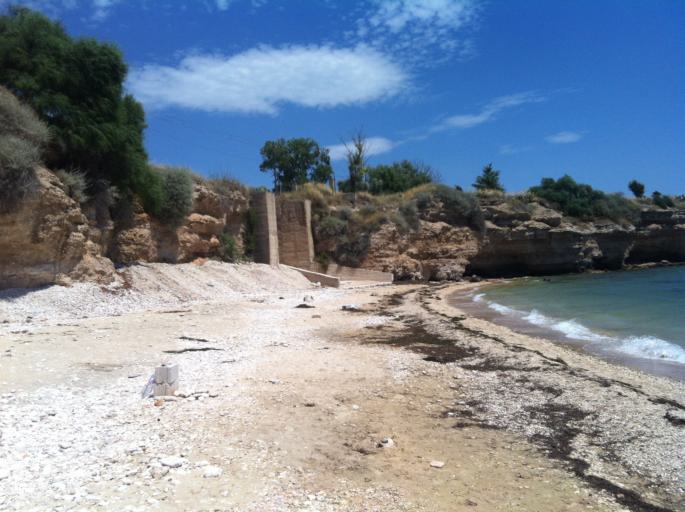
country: IT
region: Apulia
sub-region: Provincia di Foggia
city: Manfredonia
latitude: 41.6479
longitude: 15.9559
